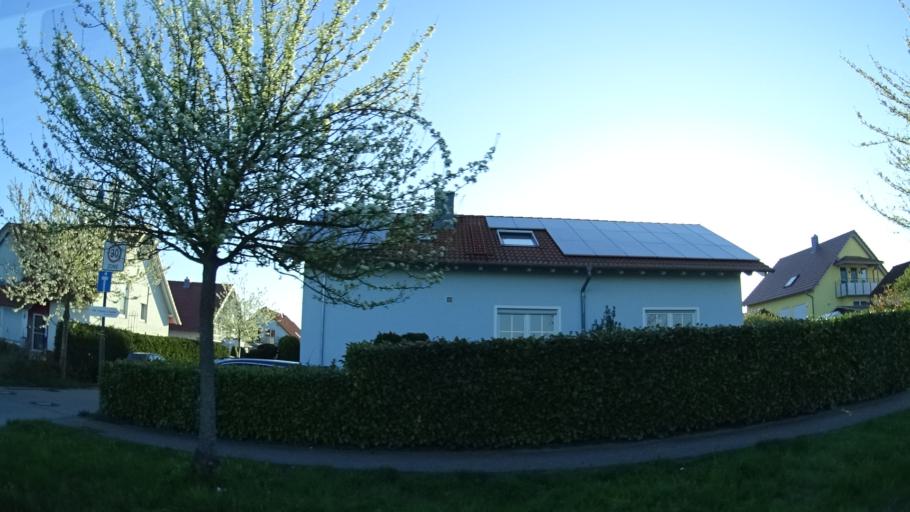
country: DE
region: Baden-Wuerttemberg
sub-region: Regierungsbezirk Stuttgart
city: Wolpertshausen
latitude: 49.1700
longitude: 9.8483
